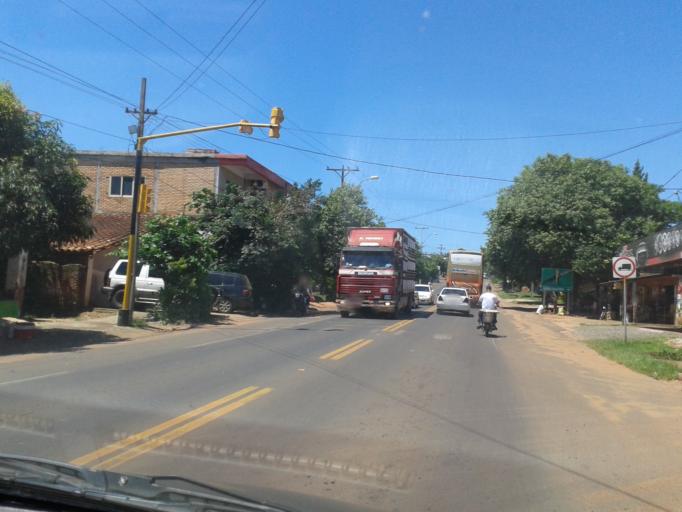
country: PY
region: Misiones
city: Santa Maria
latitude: -26.8856
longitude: -57.0149
